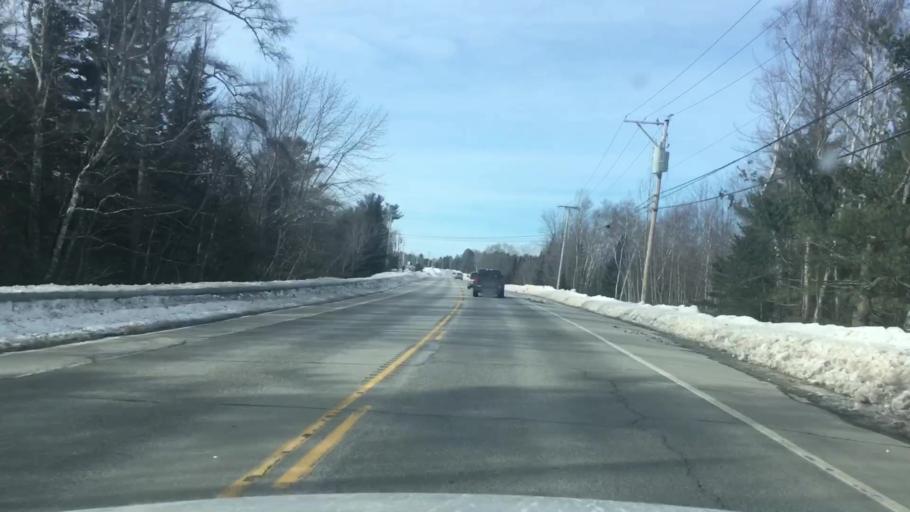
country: US
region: Maine
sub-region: Penobscot County
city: Kenduskeag
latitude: 44.9482
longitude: -68.9461
